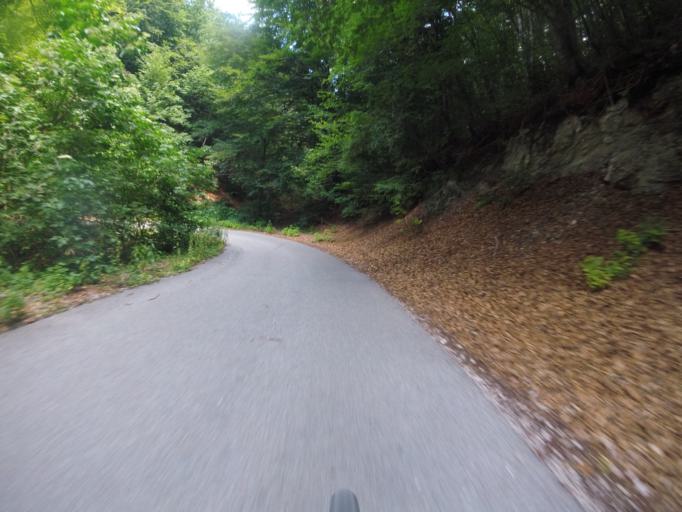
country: SI
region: Kostanjevica na Krki
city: Kostanjevica na Krki
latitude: 45.7658
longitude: 15.4043
